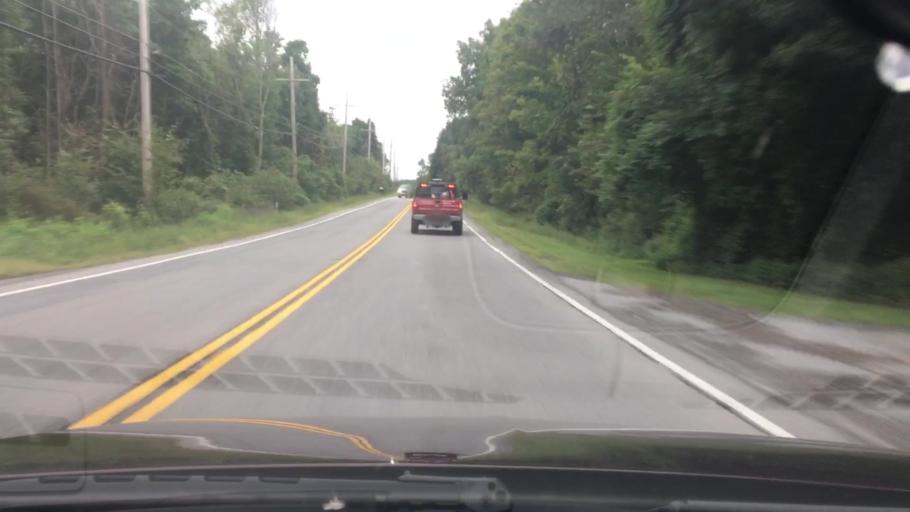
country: US
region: New York
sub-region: Dutchess County
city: Pleasant Valley
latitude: 41.7623
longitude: -73.7815
